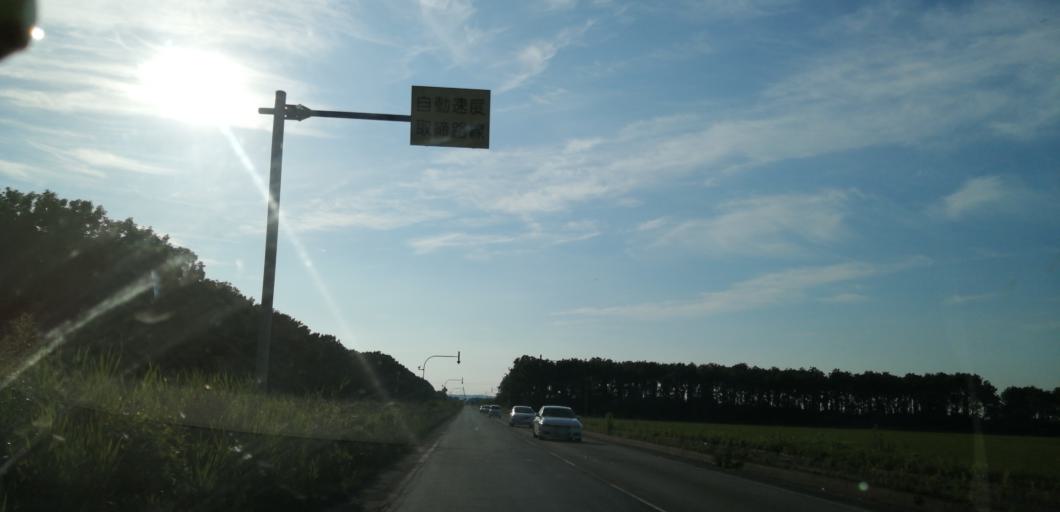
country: JP
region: Hokkaido
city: Kitahiroshima
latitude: 42.9776
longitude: 141.6427
